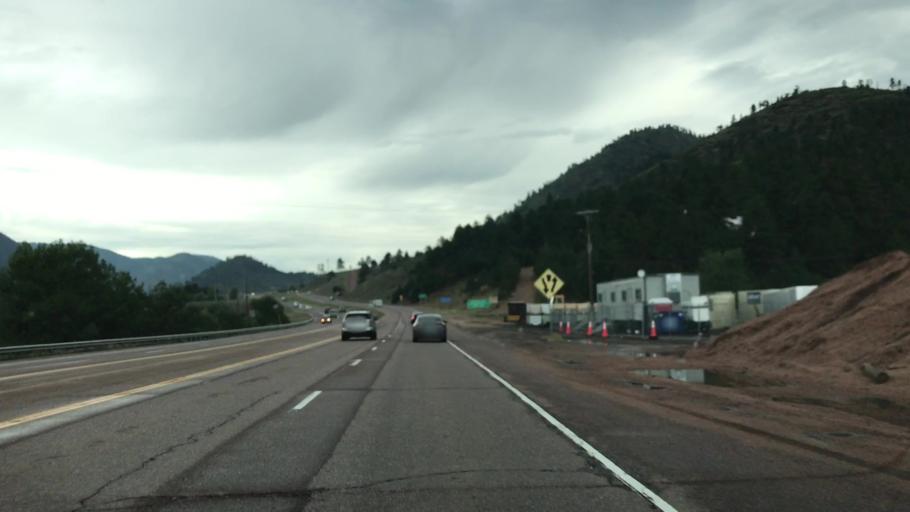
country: US
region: Colorado
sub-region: El Paso County
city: Cascade-Chipita Park
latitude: 38.9175
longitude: -104.9832
